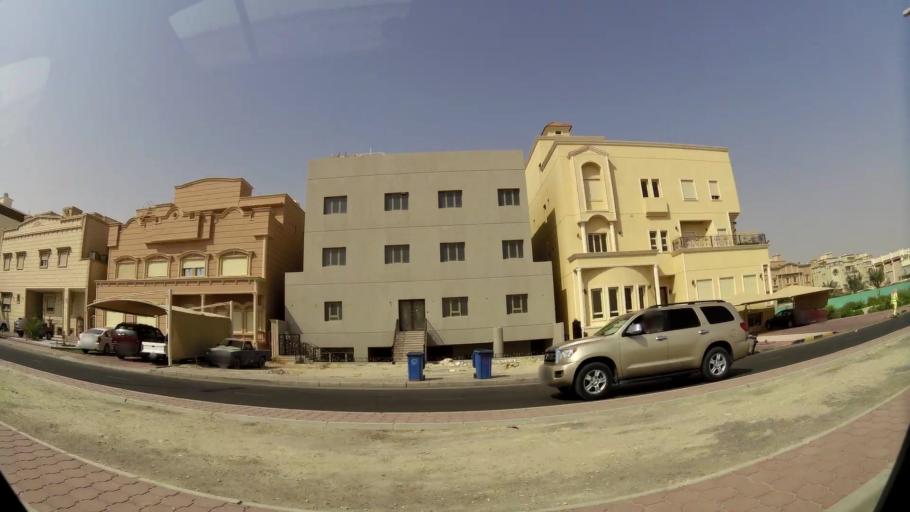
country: KW
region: Muhafazat al Jahra'
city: Al Jahra'
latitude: 29.3213
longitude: 47.7431
